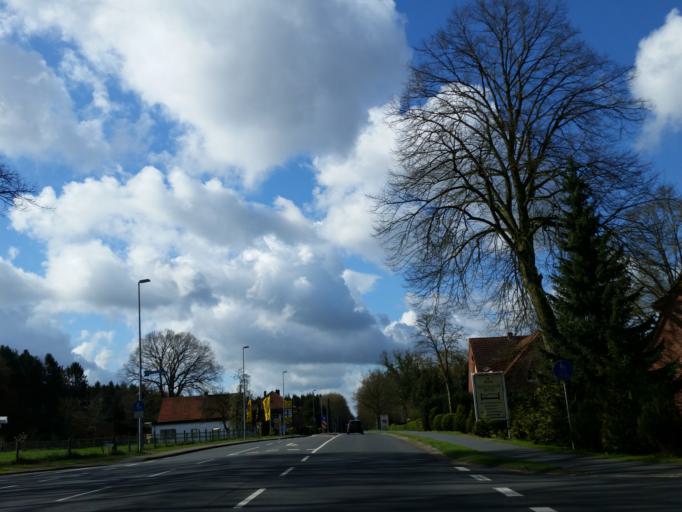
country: DE
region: Lower Saxony
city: Ahausen
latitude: 53.0784
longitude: 9.3560
